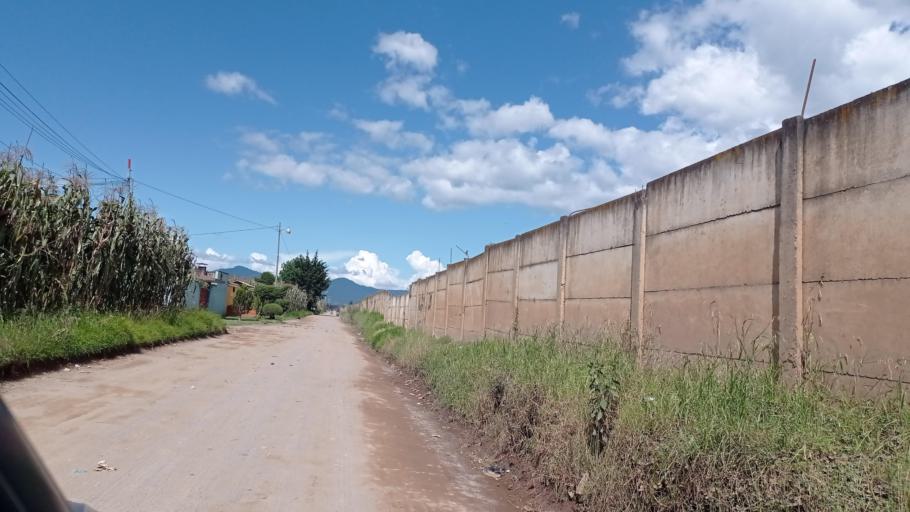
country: GT
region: Quetzaltenango
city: Olintepeque
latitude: 14.8704
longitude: -91.4980
